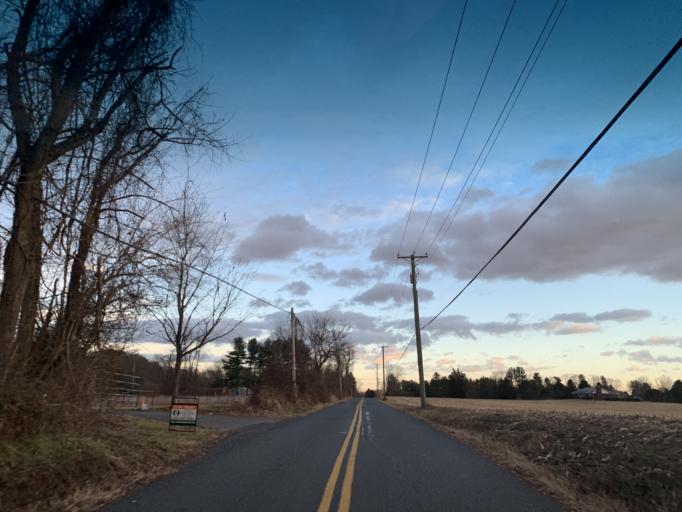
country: US
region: Pennsylvania
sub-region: York County
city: Susquehanna Trails
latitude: 39.6609
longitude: -76.3146
